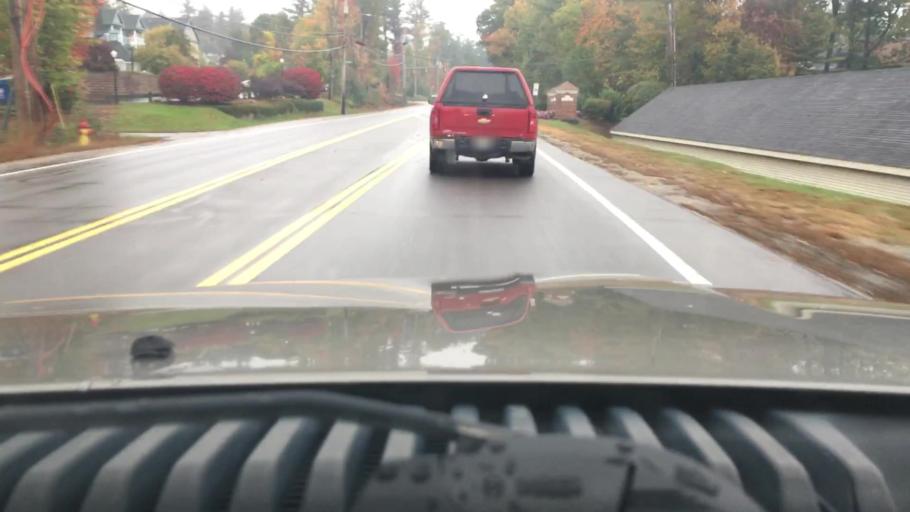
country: US
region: New Hampshire
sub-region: Hillsborough County
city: Pinardville
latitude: 43.0344
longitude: -71.4822
